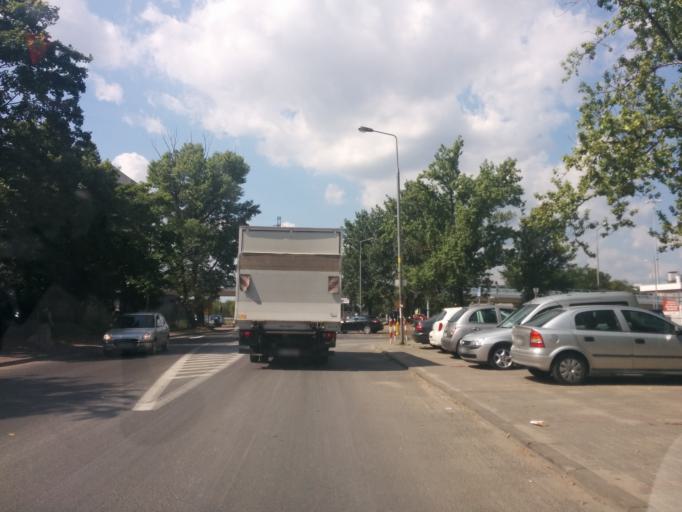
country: PL
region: Masovian Voivodeship
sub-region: Warszawa
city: Zoliborz
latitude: 52.2939
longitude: 21.0015
